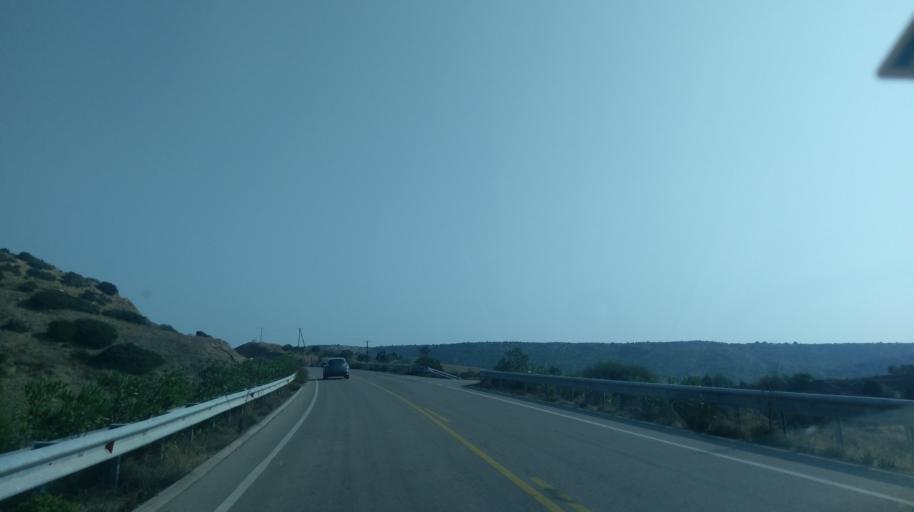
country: CY
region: Ammochostos
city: Leonarisso
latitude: 35.4776
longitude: 34.1167
